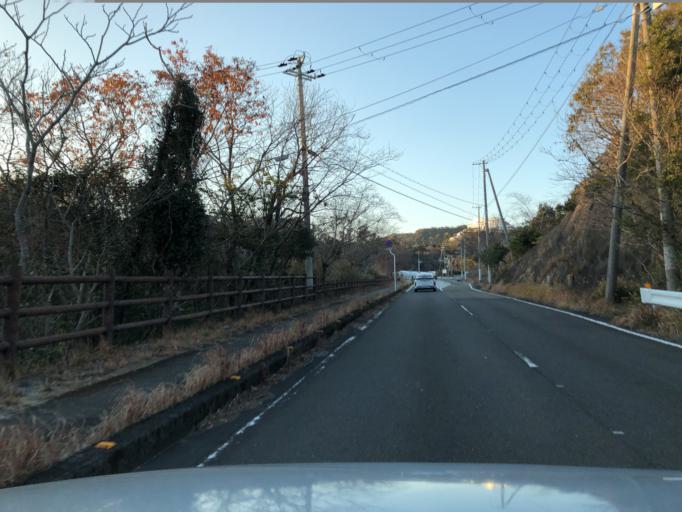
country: JP
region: Wakayama
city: Tanabe
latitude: 33.6617
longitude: 135.3753
